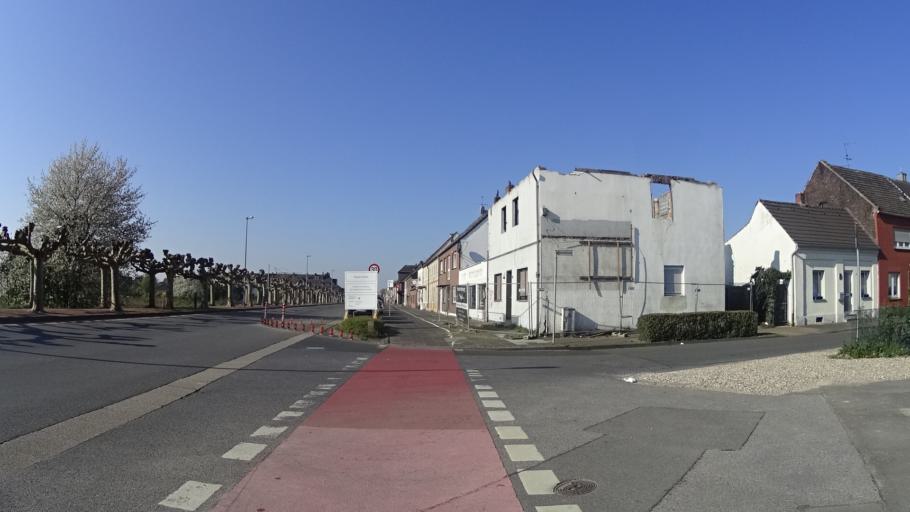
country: DE
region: North Rhine-Westphalia
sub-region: Regierungsbezirk Dusseldorf
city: Wesel
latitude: 51.6312
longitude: 6.5836
